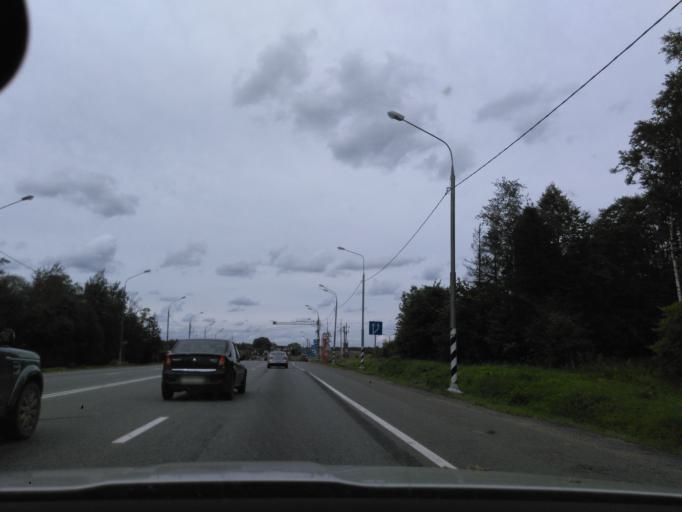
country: RU
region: Moskovskaya
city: Klin
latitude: 56.2978
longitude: 36.7995
